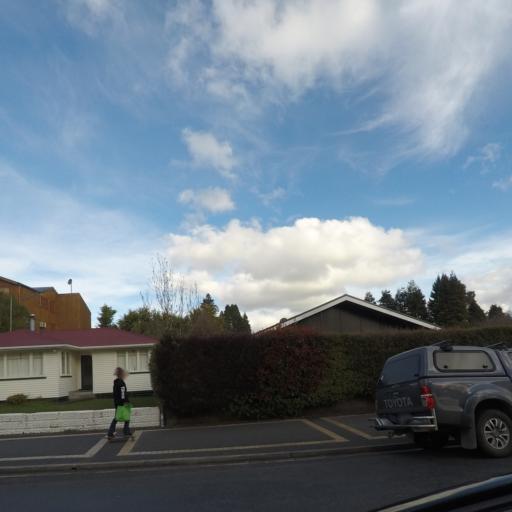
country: NZ
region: Manawatu-Wanganui
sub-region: Ruapehu District
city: Waiouru
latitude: -39.4020
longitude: 175.4121
